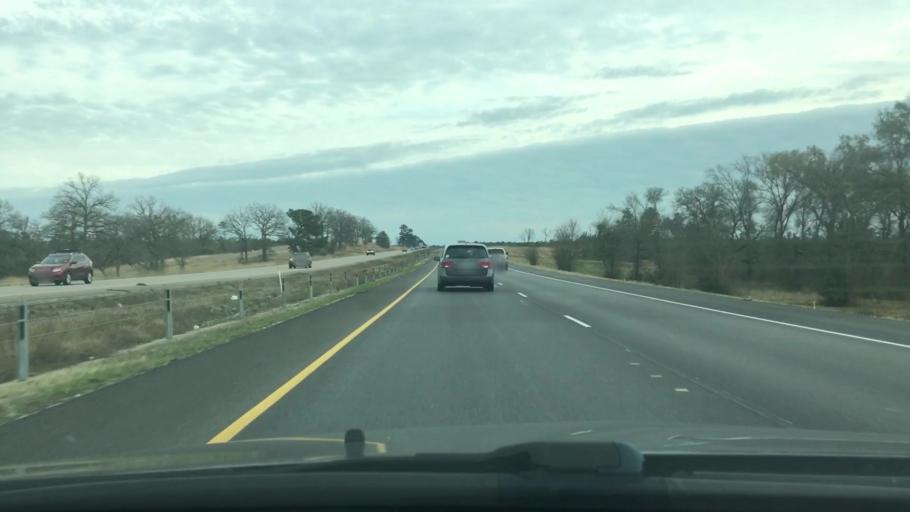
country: US
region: Texas
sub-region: Madison County
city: Madisonville
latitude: 30.8482
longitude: -95.7342
